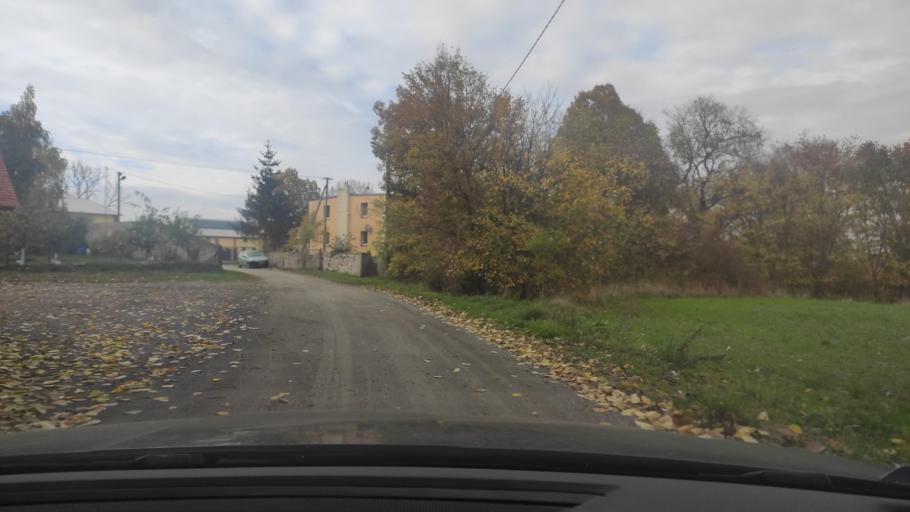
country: PL
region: Greater Poland Voivodeship
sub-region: Powiat poznanski
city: Kostrzyn
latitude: 52.4485
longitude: 17.2119
